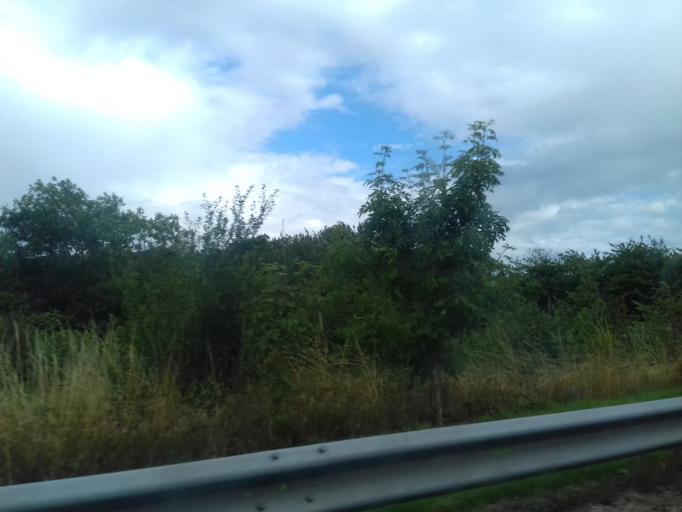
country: IE
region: Munster
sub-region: Waterford
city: Waterford
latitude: 52.2576
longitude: -7.1808
